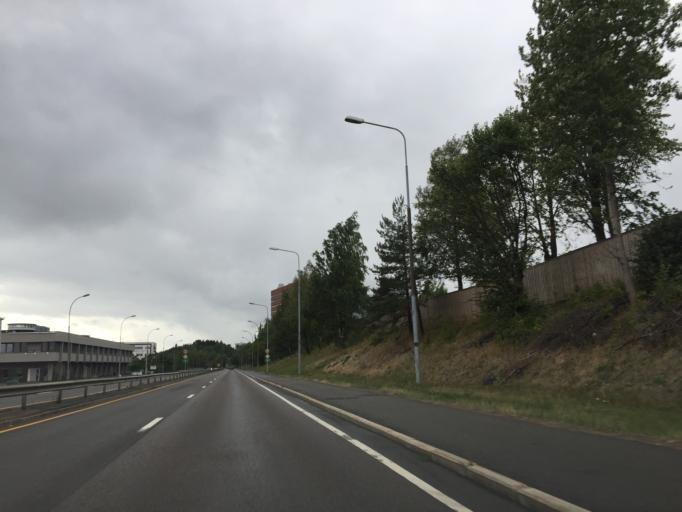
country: NO
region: Akershus
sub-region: Lorenskog
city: Kjenn
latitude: 59.9400
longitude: 10.8502
